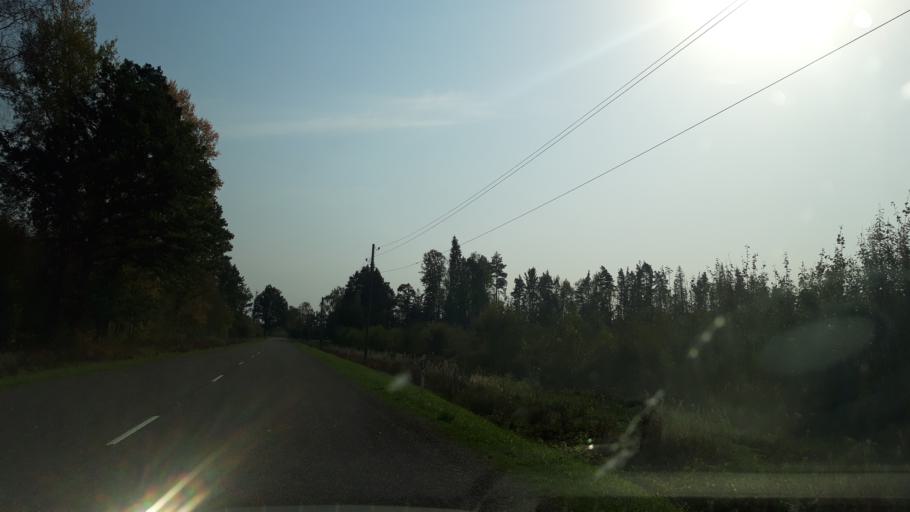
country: LV
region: Burtnieki
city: Matisi
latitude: 57.6290
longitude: 25.2648
